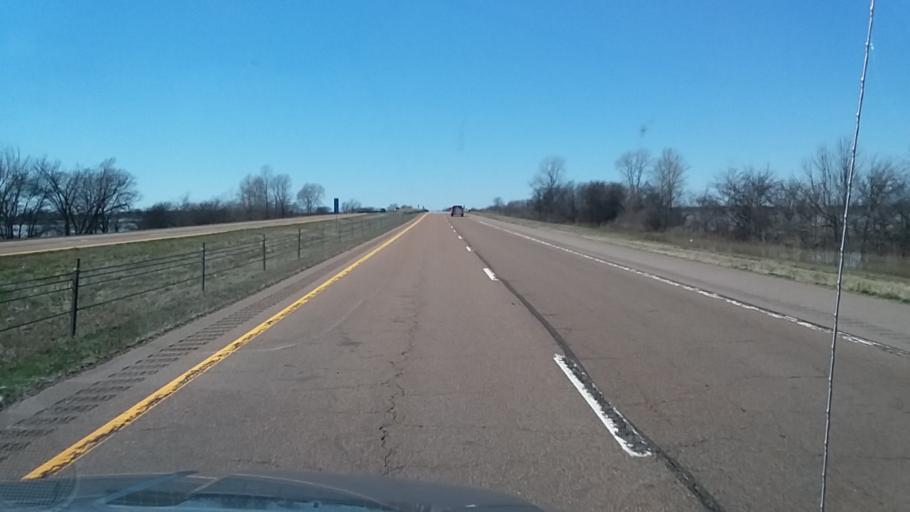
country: US
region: Missouri
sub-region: Pemiscot County
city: Caruthersville
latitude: 36.0846
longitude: -89.5464
